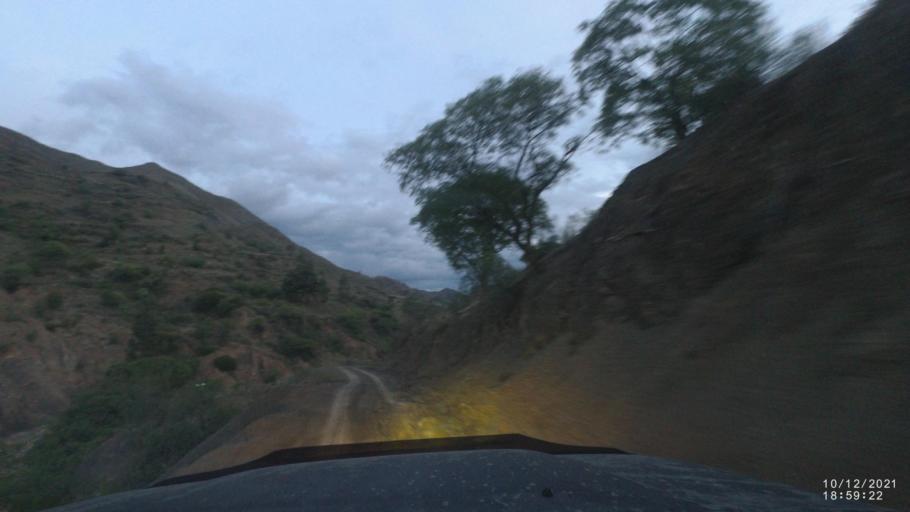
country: BO
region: Cochabamba
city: Tarata
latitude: -17.8932
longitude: -65.9510
